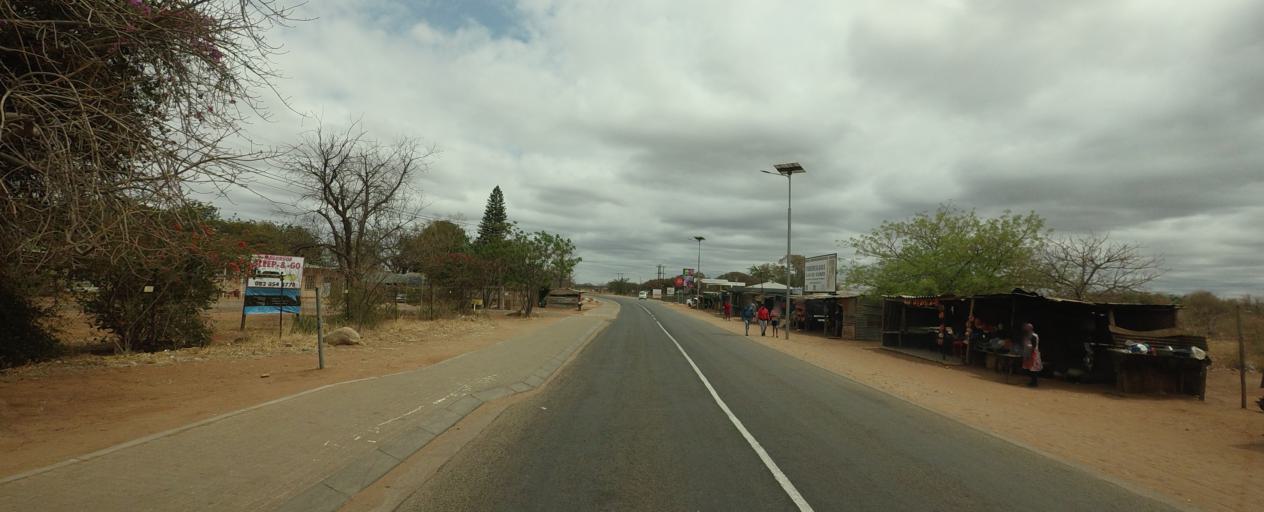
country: BW
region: Central
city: Mathathane
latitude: -22.6785
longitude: 29.1042
